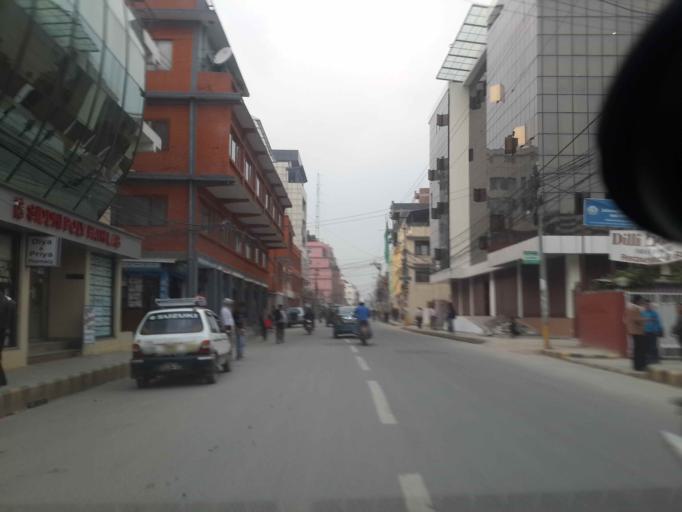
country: NP
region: Central Region
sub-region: Bagmati Zone
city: Kathmandu
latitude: 27.7072
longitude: 85.3272
